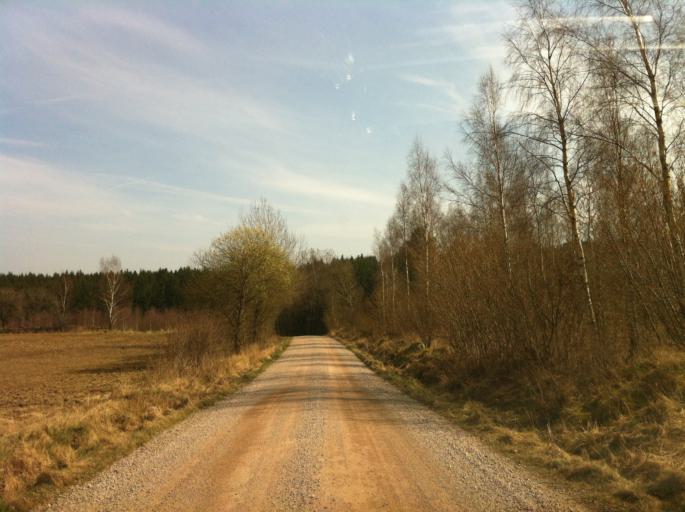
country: SE
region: Skane
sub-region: Klippans Kommun
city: Ljungbyhed
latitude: 55.9991
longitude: 13.3044
